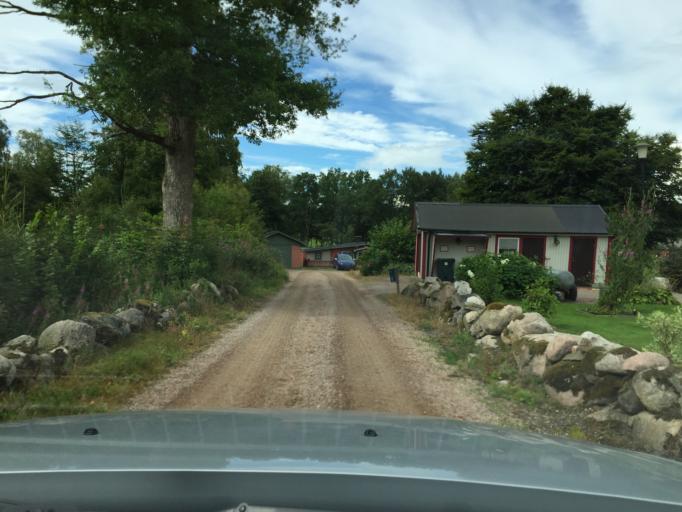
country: SE
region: Skane
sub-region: Hassleholms Kommun
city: Sosdala
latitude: 56.0301
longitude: 13.6384
